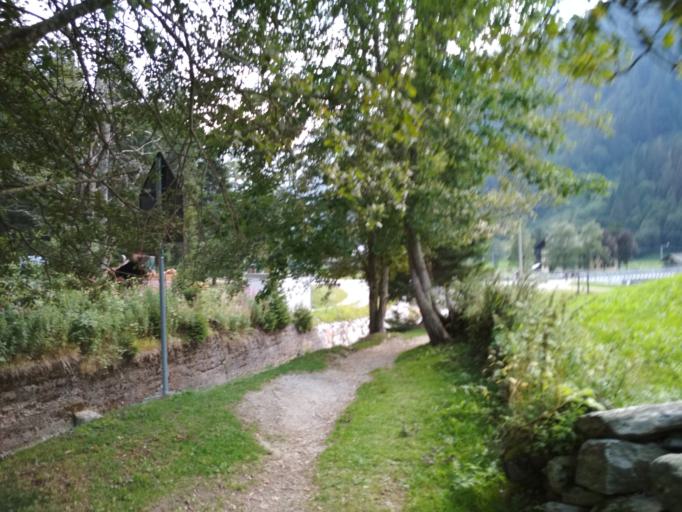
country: IT
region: Aosta Valley
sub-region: Valle d'Aosta
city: Gressoney-Saint-Jean
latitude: 45.7943
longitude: 7.8244
